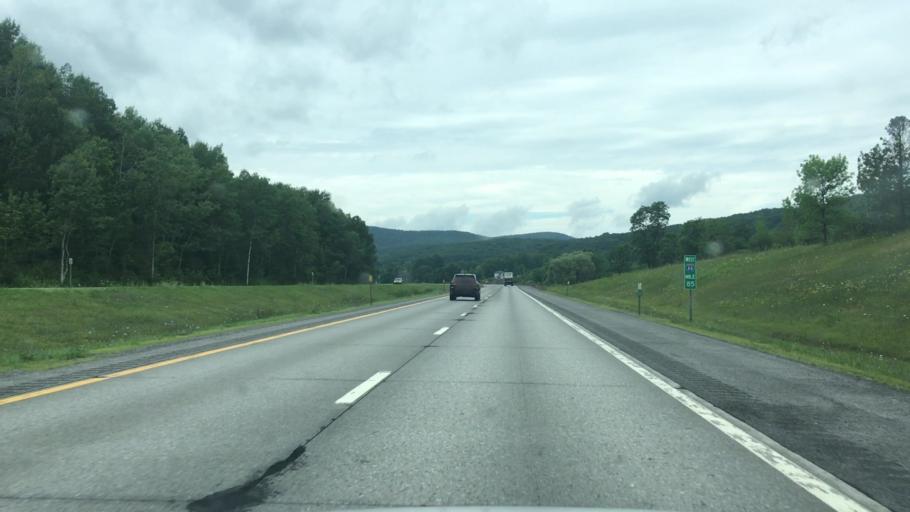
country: US
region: New York
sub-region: Schoharie County
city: Cobleskill
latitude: 42.6466
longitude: -74.5939
